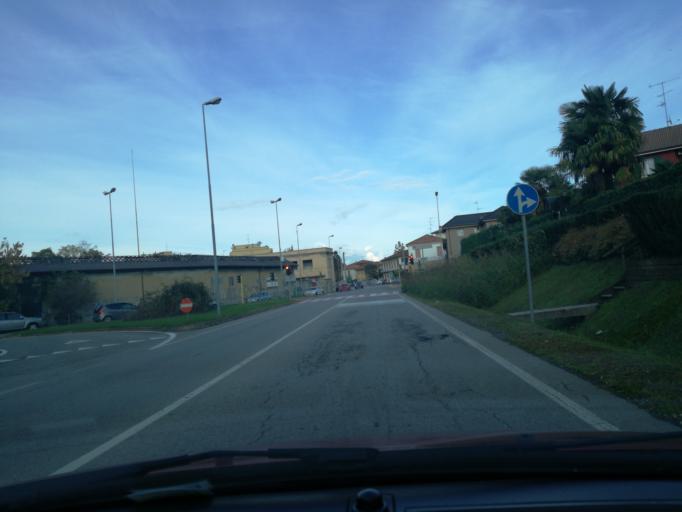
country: IT
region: Lombardy
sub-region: Provincia di Monza e Brianza
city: Vimercate
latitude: 45.6095
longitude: 9.3765
